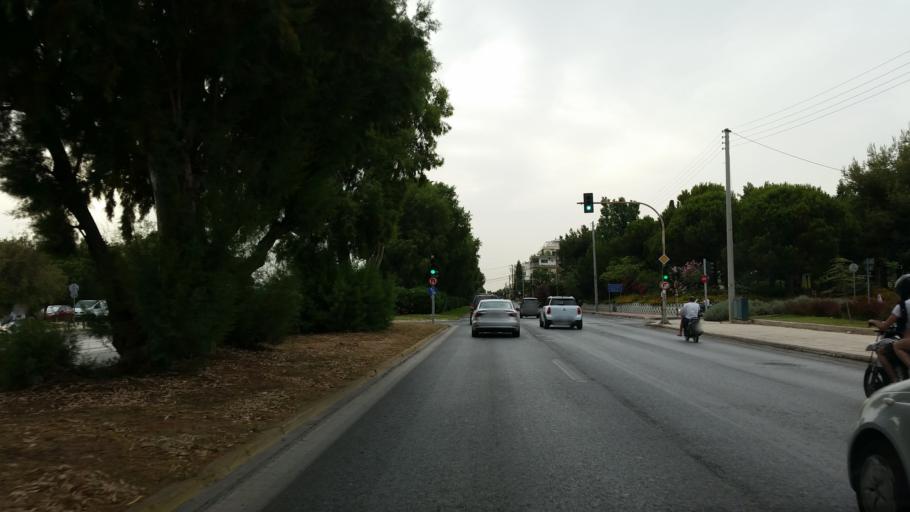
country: GR
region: Attica
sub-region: Nomarchia Anatolikis Attikis
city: Voula
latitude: 37.8389
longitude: 23.7627
